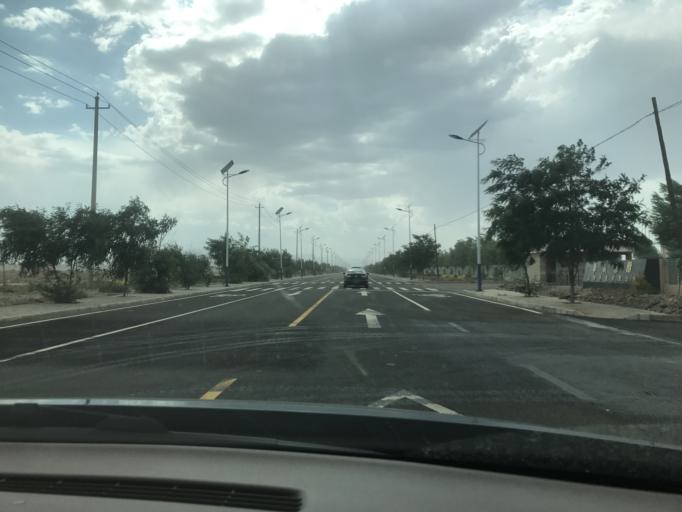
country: CN
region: Gansu Sheng
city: Wuwei
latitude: 38.1031
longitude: 102.4540
